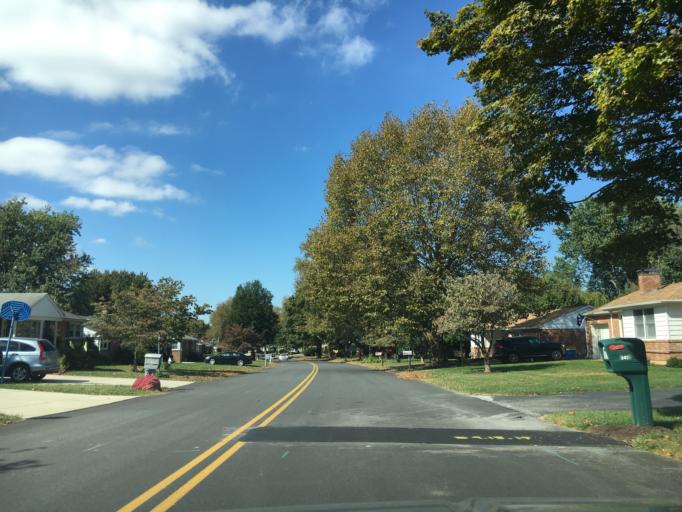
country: US
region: Pennsylvania
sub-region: York County
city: East York
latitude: 39.9667
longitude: -76.6760
